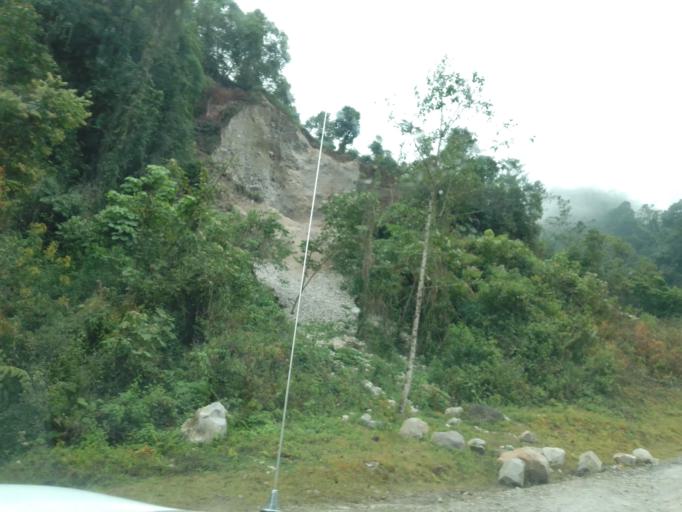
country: MX
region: Chiapas
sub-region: Union Juarez
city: Santo Domingo
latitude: 15.0930
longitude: -92.0937
